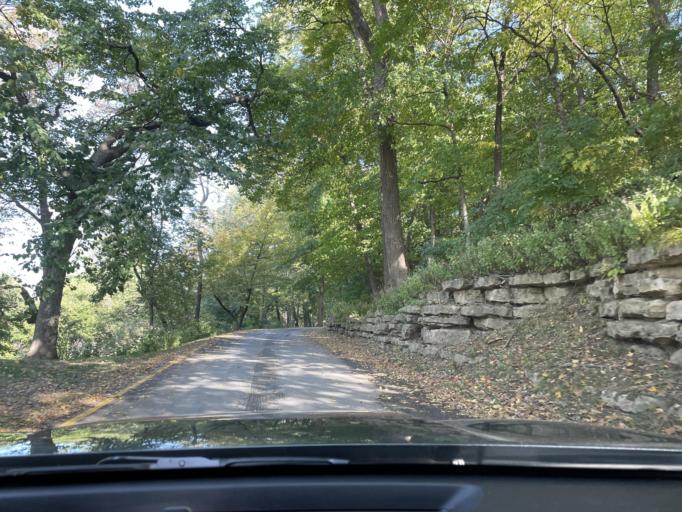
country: US
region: Kansas
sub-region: Doniphan County
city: Elwood
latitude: 39.7103
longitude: -94.8552
